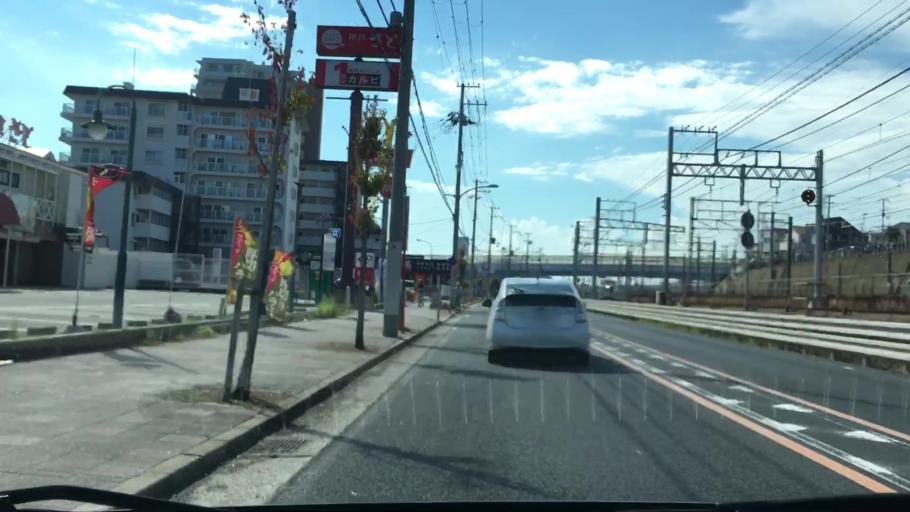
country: JP
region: Hyogo
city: Akashi
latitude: 34.6446
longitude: 135.0147
